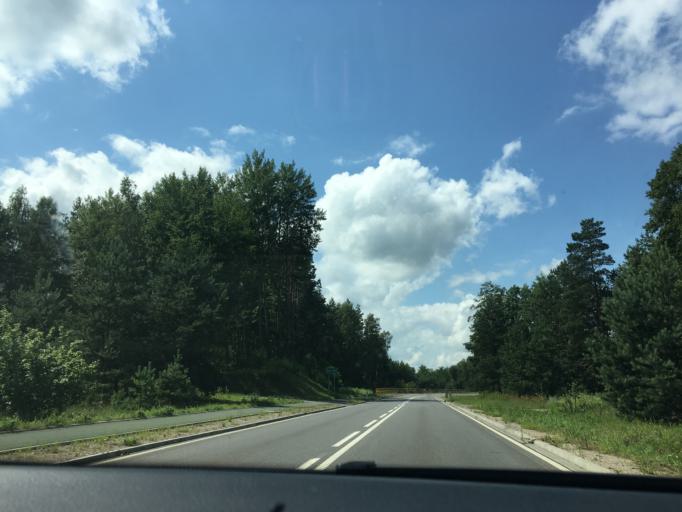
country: PL
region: Podlasie
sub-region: Powiat sejnenski
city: Krasnopol
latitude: 54.0908
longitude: 23.1399
